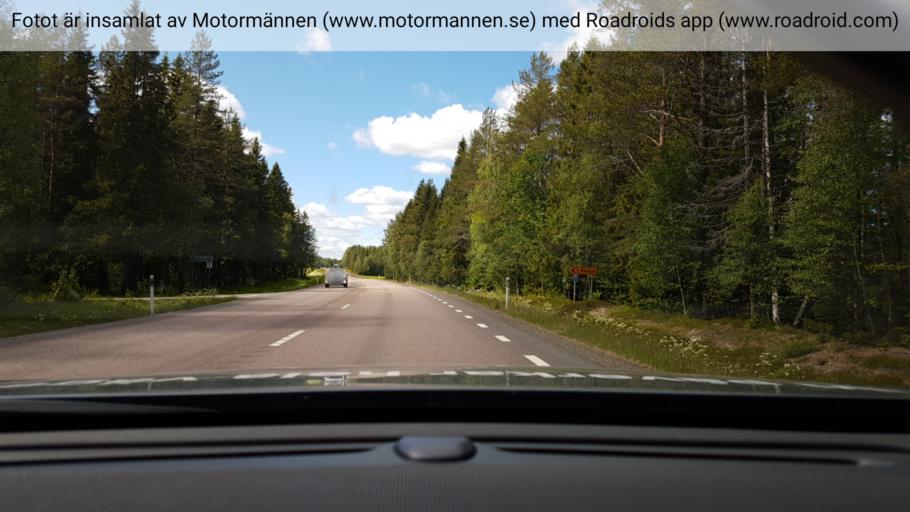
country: SE
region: Vaesterbotten
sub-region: Skelleftea Kommun
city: Burea
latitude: 64.3343
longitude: 21.2517
